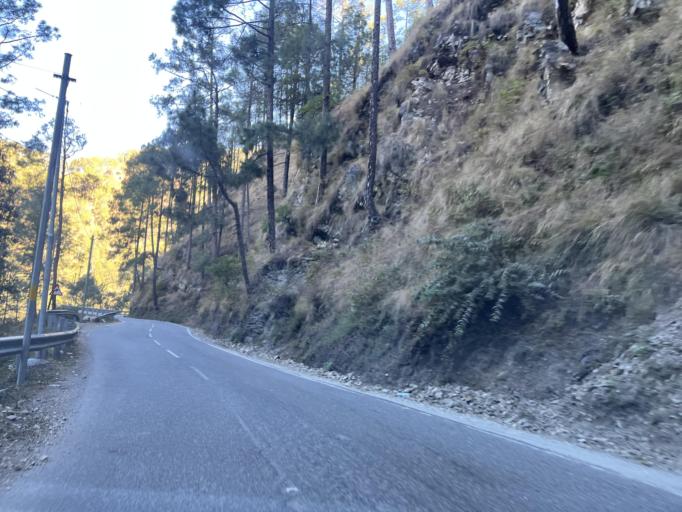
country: IN
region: Uttarakhand
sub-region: Naini Tal
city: Bhowali
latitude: 29.4024
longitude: 79.5107
